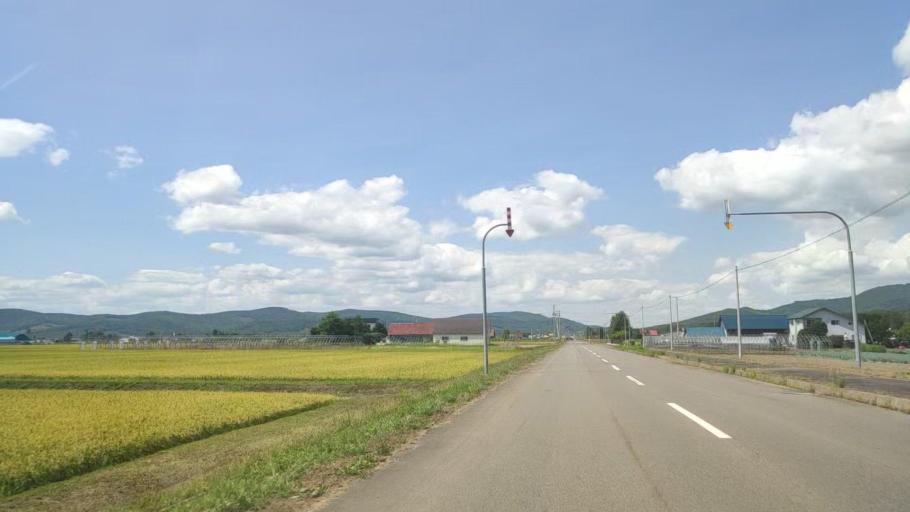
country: JP
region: Hokkaido
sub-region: Asahikawa-shi
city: Asahikawa
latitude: 43.8965
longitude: 142.5164
